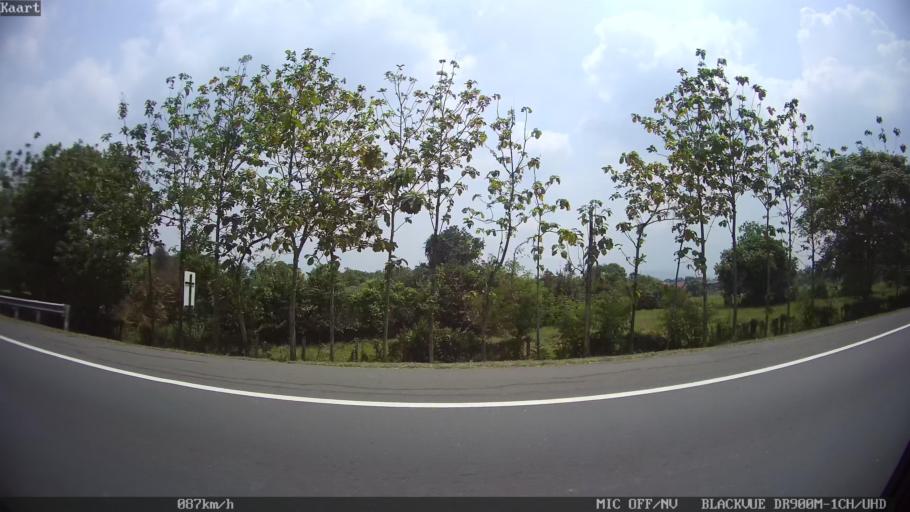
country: ID
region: Banten
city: Serang
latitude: -6.0833
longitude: 106.1349
